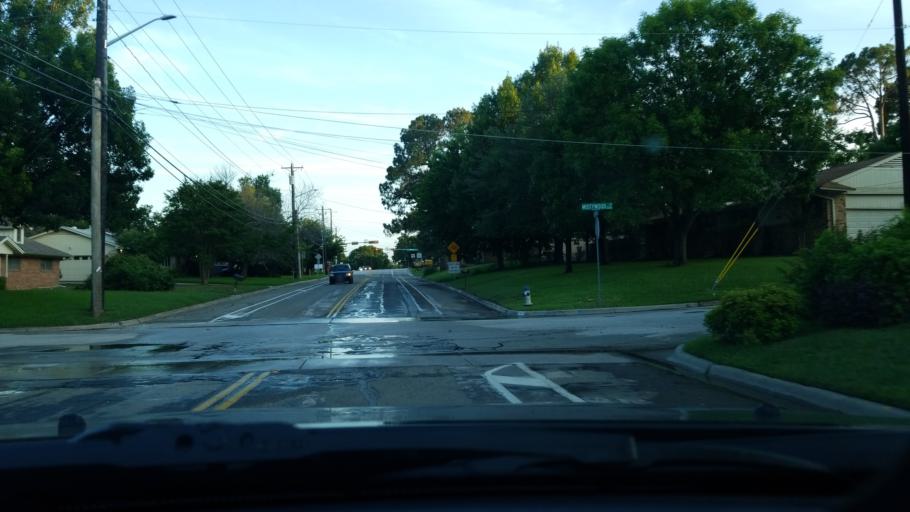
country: US
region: Texas
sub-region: Denton County
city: Denton
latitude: 33.2374
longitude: -97.1068
